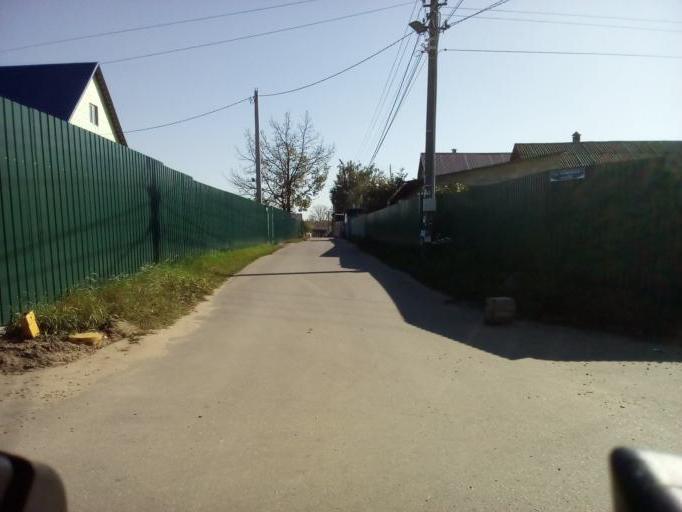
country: RU
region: Moskovskaya
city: Ramenskoye
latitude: 55.5488
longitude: 38.2856
